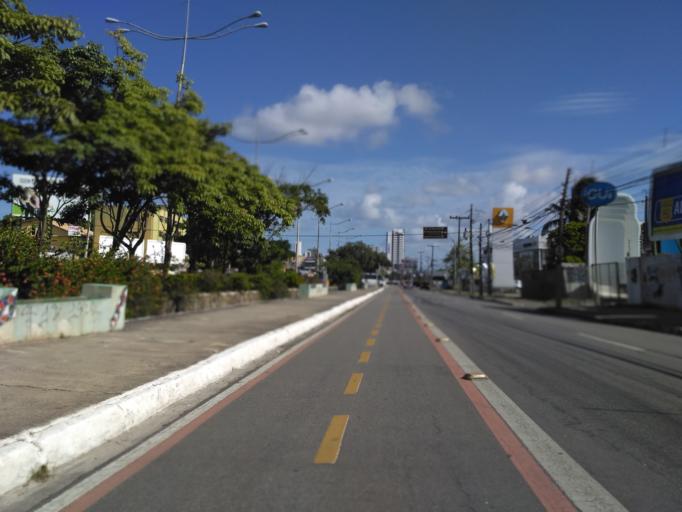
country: BR
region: Pernambuco
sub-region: Jaboatao Dos Guararapes
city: Jaboatao
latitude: -8.1639
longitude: -34.9151
